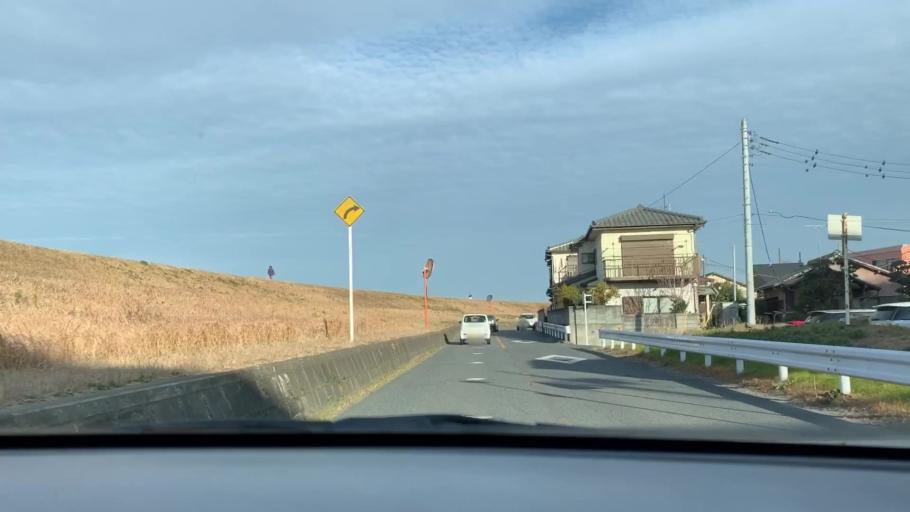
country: JP
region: Chiba
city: Matsudo
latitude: 35.7922
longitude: 139.8917
